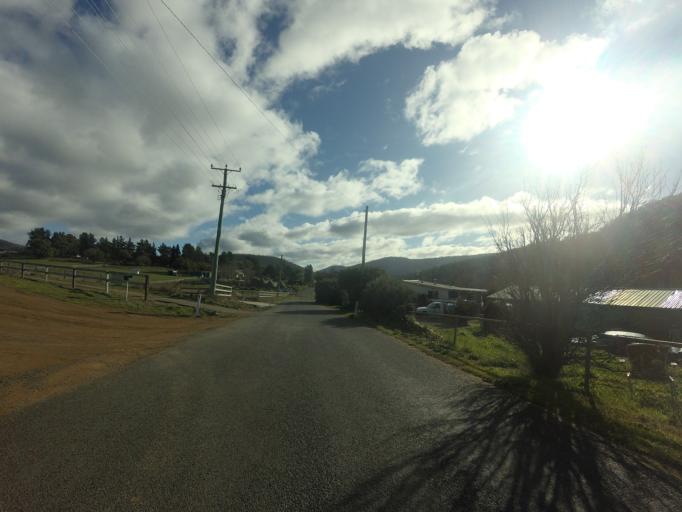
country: AU
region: Tasmania
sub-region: Derwent Valley
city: New Norfolk
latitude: -42.7995
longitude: 147.1359
